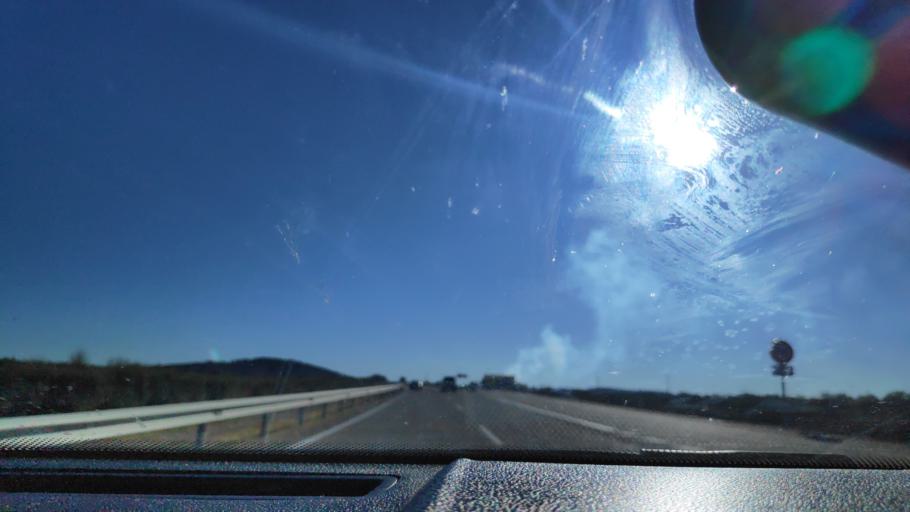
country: ES
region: Extremadura
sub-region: Provincia de Badajoz
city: Los Santos de Maimona
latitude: 38.4757
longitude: -6.3602
